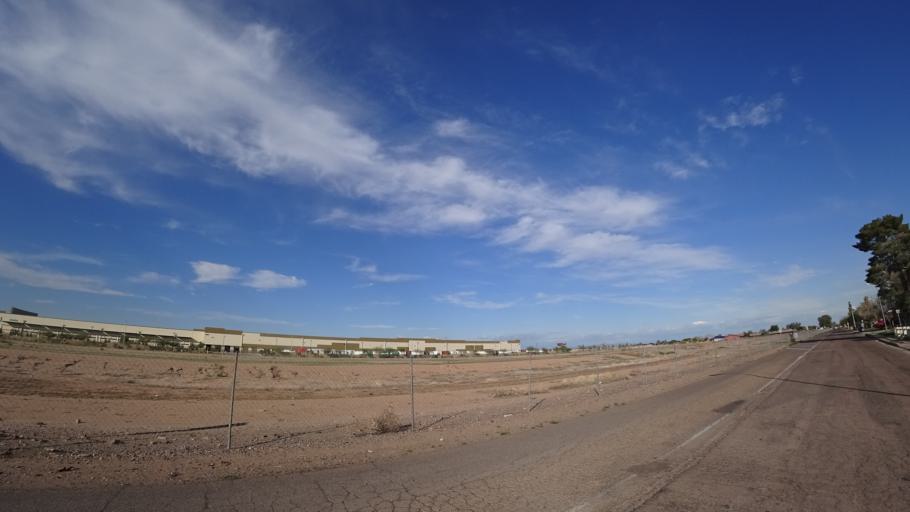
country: US
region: Arizona
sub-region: Maricopa County
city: Tolleson
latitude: 33.4587
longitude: -112.2001
